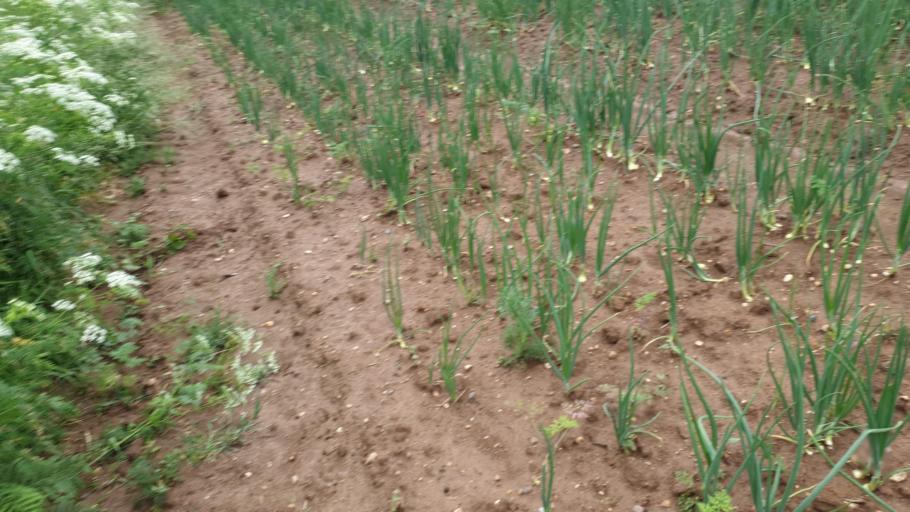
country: GB
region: England
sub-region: Essex
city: Alresford
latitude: 51.8606
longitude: 1.0321
